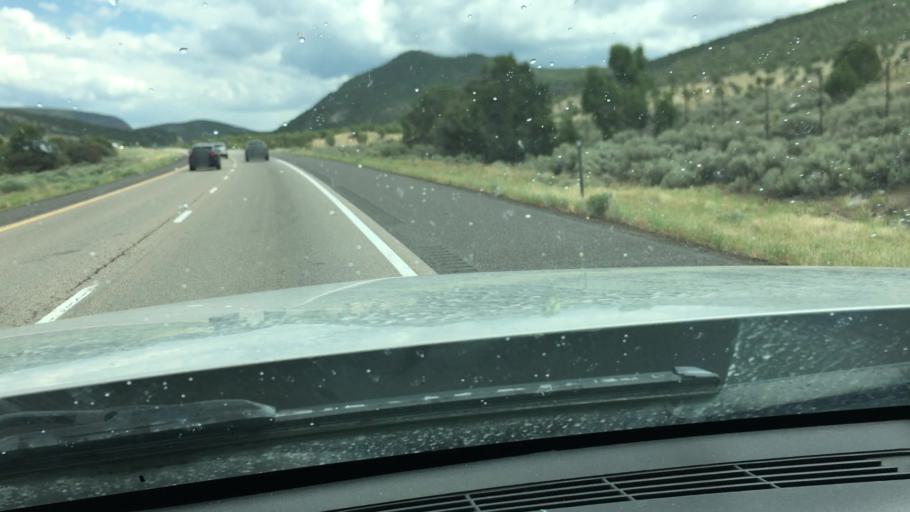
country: US
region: Utah
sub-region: Beaver County
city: Beaver
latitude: 38.1915
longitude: -112.6434
